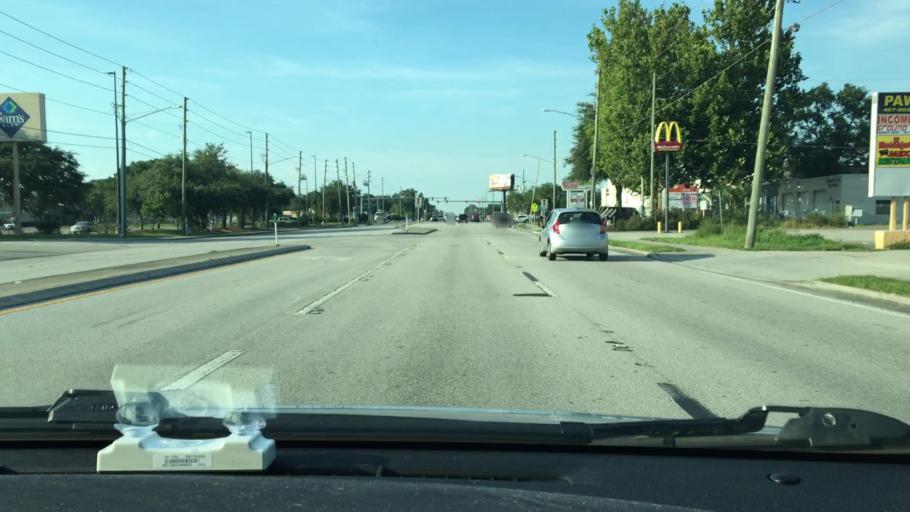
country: US
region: Florida
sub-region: Orange County
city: Union Park
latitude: 28.5707
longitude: -81.2861
